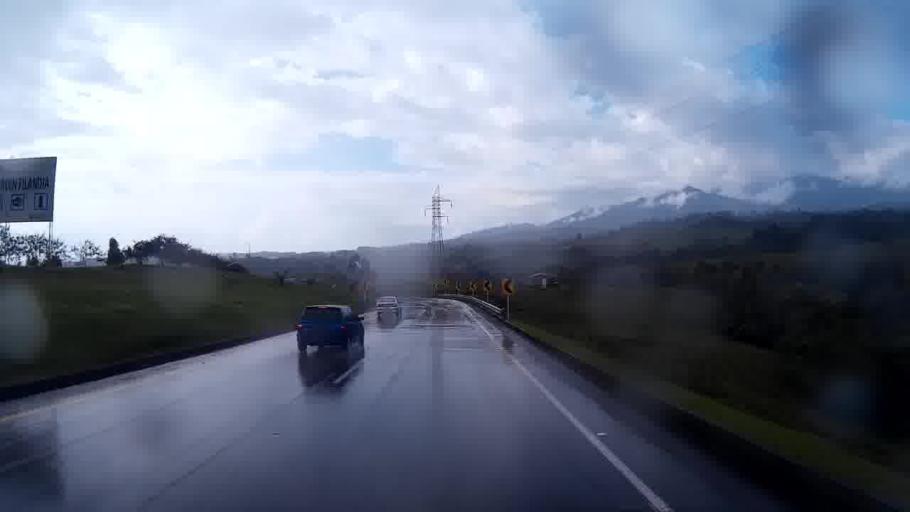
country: CO
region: Quindio
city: Filandia
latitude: 4.6868
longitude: -75.6064
